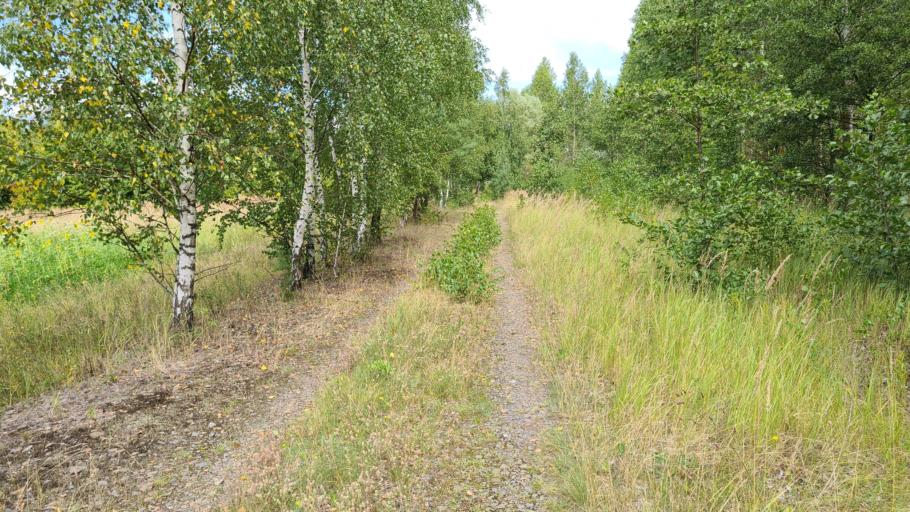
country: DE
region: Brandenburg
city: Spremberg
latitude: 51.5844
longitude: 14.3097
